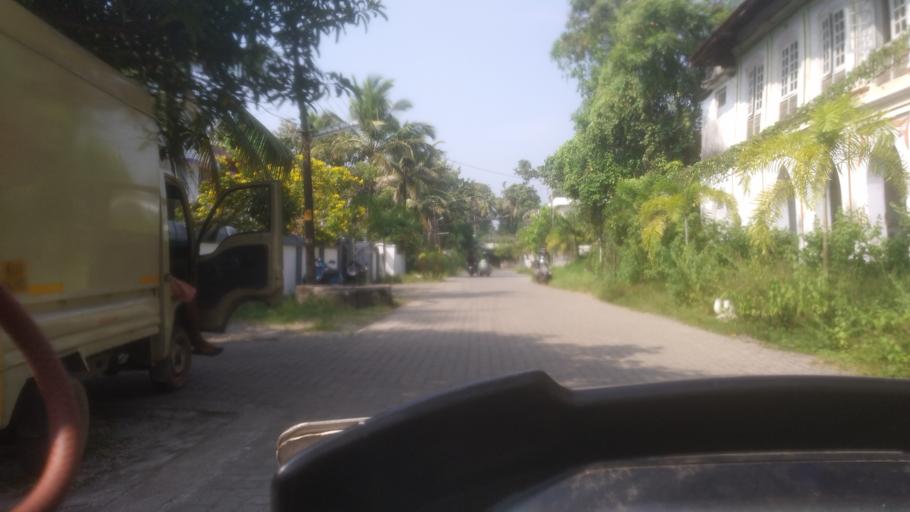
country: IN
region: Kerala
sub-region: Ernakulam
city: Elur
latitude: 10.0496
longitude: 76.2208
